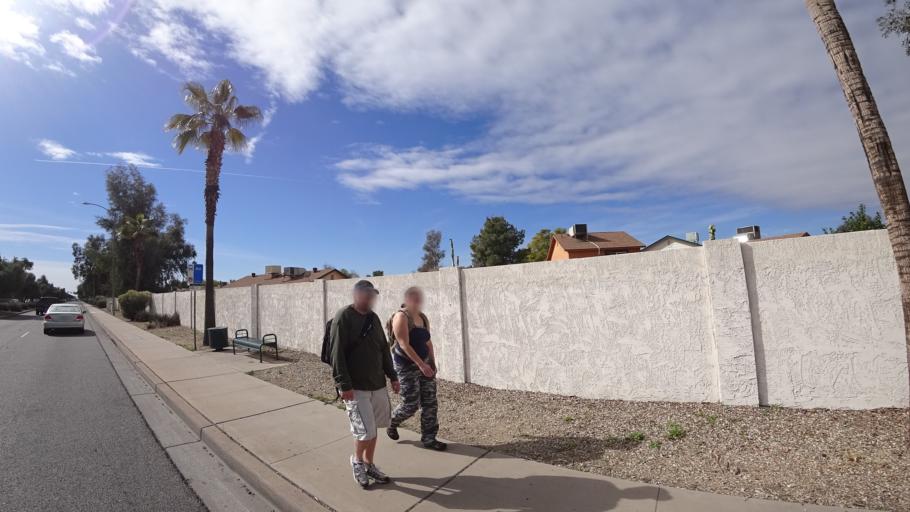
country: US
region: Arizona
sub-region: Maricopa County
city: Peoria
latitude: 33.6206
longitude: -112.1859
